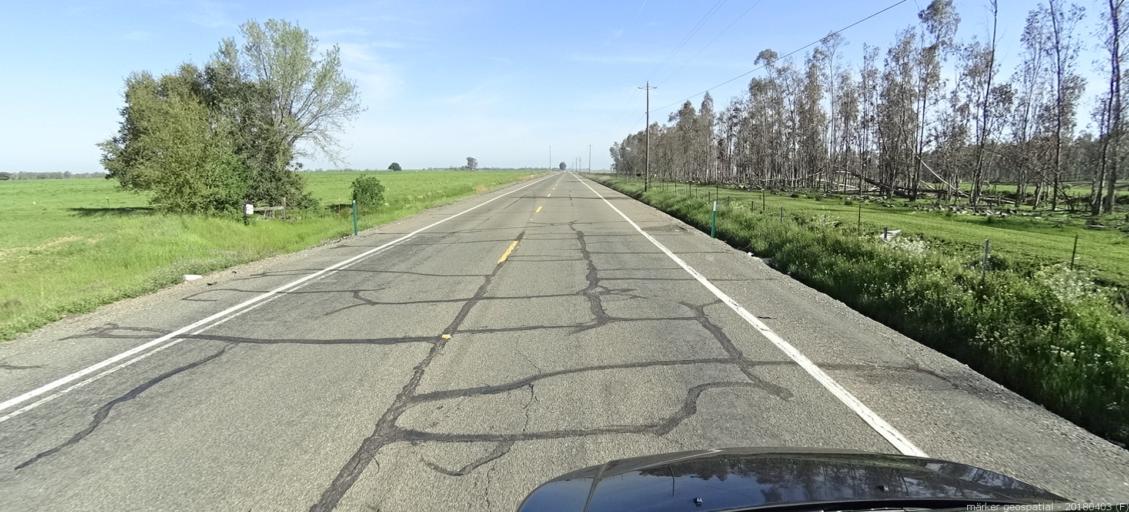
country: US
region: California
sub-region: Sacramento County
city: Clay
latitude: 38.3548
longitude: -121.1684
